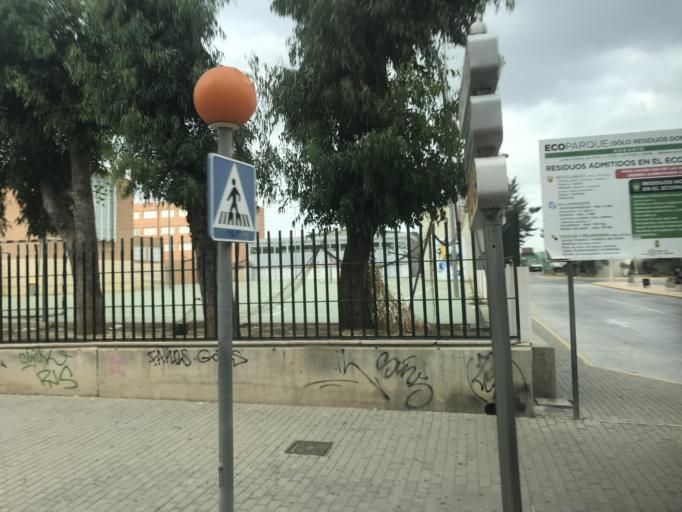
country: ES
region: Valencia
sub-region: Provincia de Alicante
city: Guardamar del Segura
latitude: 38.0877
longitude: -0.6557
